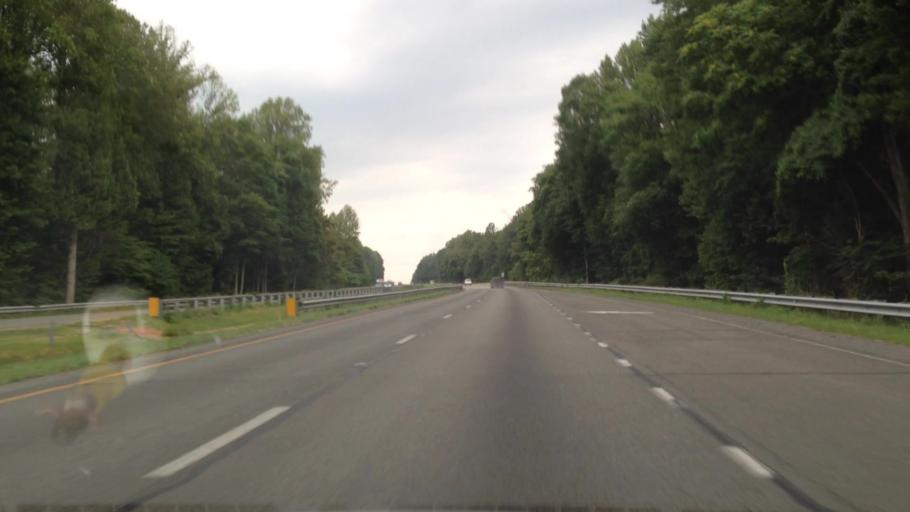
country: US
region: North Carolina
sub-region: Surry County
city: Pilot Mountain
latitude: 36.3404
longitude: -80.4582
